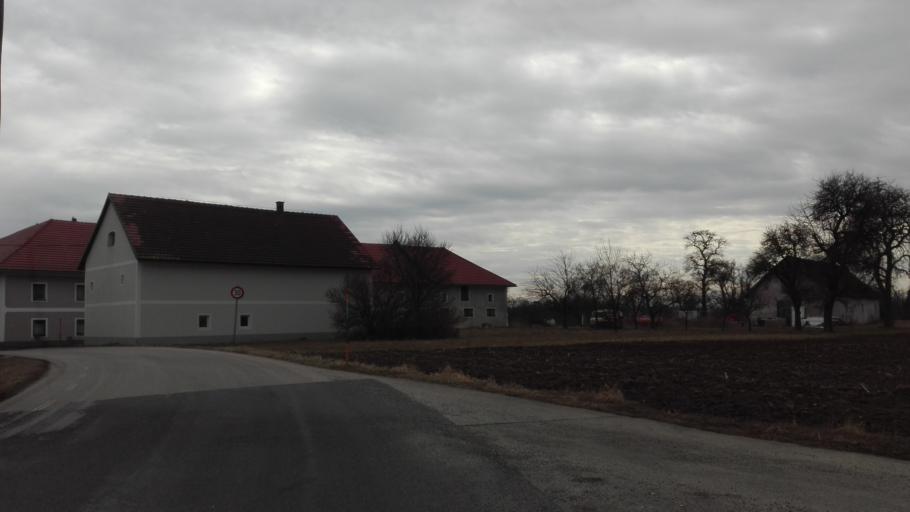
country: AT
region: Upper Austria
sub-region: Politischer Bezirk Linz-Land
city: Traun
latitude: 48.2396
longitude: 14.2189
